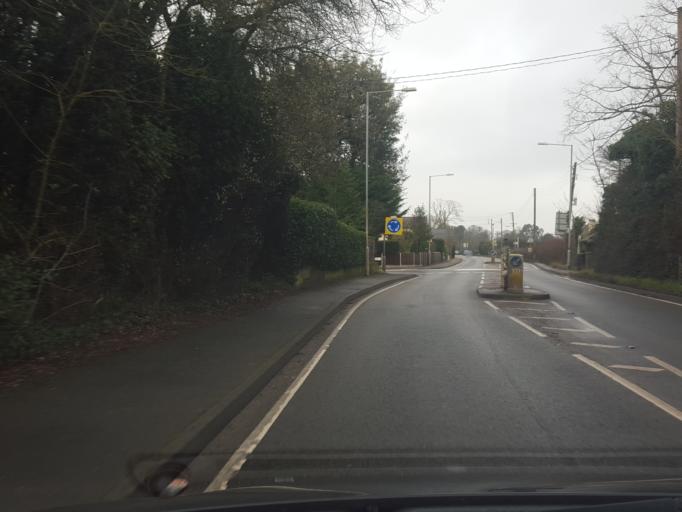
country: GB
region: England
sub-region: Essex
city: Great Horkesley
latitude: 51.9377
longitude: 0.8757
